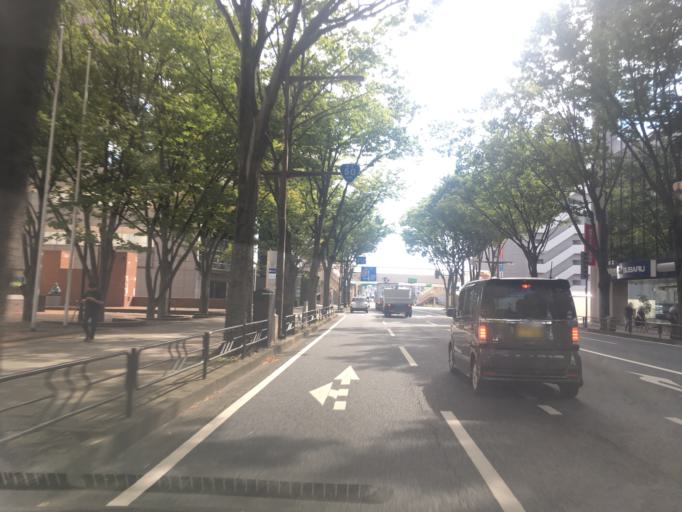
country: JP
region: Gunma
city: Maebashi-shi
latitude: 36.3895
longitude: 139.0713
